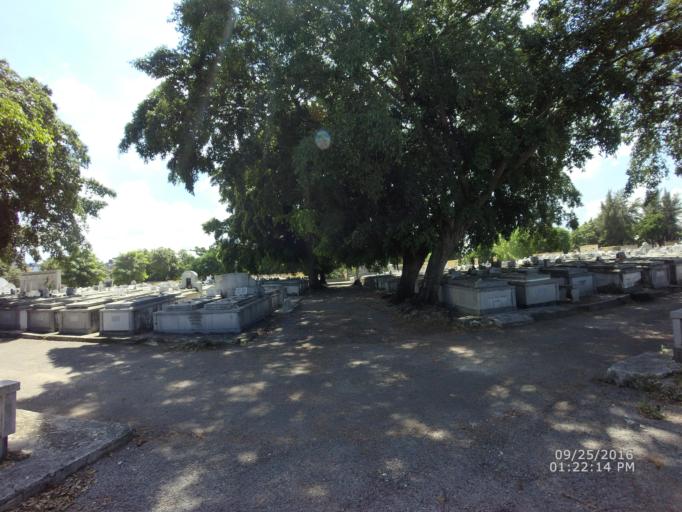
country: CU
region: La Habana
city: Havana
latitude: 23.1210
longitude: -82.4010
